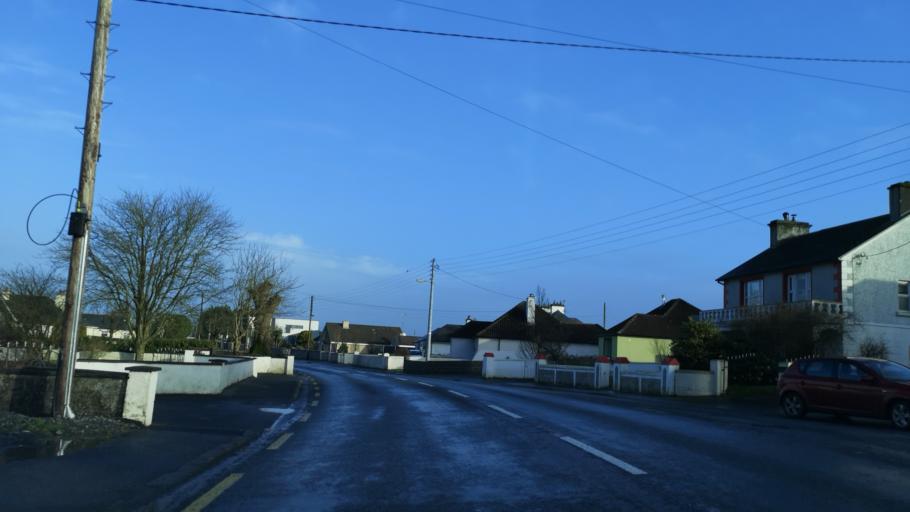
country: IE
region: Connaught
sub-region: County Galway
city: Tuam
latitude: 53.5062
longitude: -8.8362
